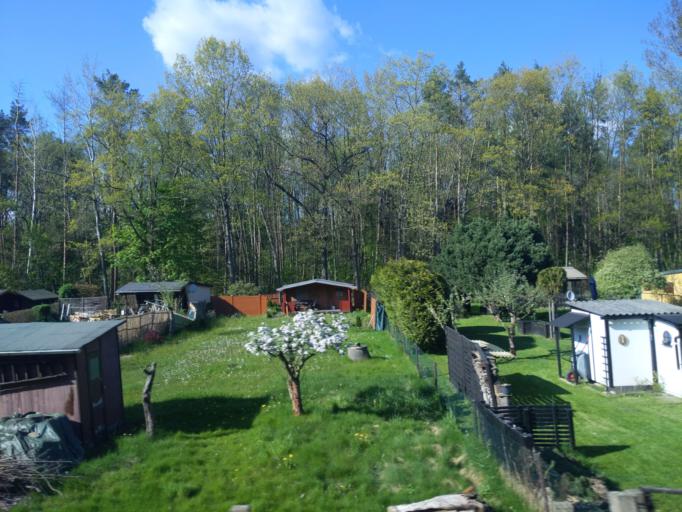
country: DE
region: Saxony
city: Arnsdorf
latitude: 51.0903
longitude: 13.9921
